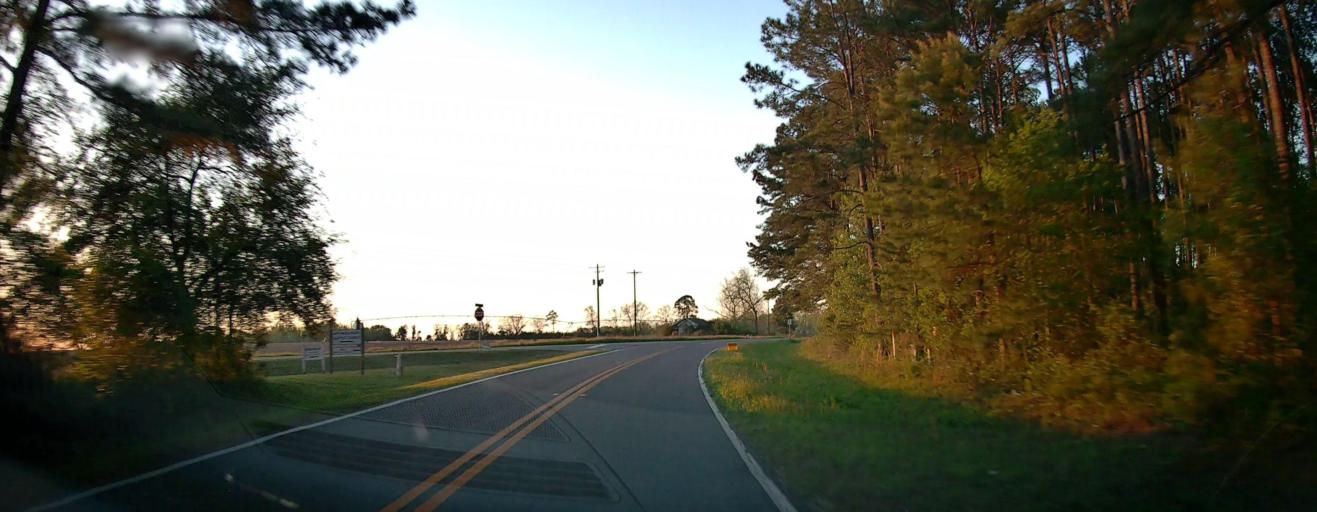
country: US
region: Georgia
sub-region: Ben Hill County
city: Fitzgerald
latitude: 31.7727
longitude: -83.3842
